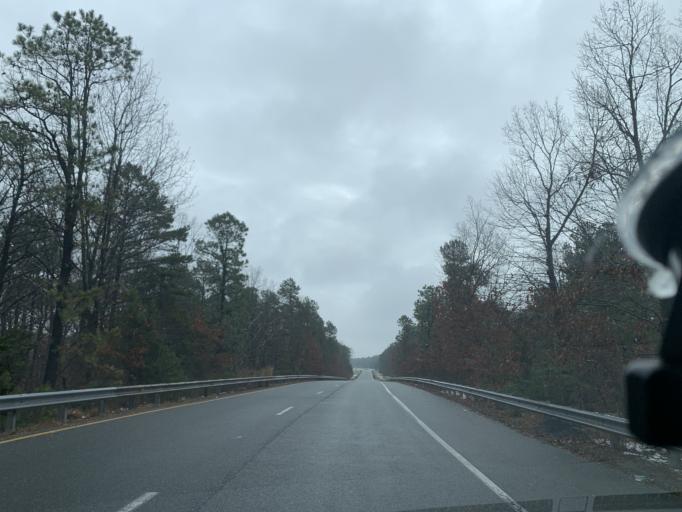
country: US
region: New Jersey
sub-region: Atlantic County
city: Pomona
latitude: 39.4494
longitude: -74.6257
